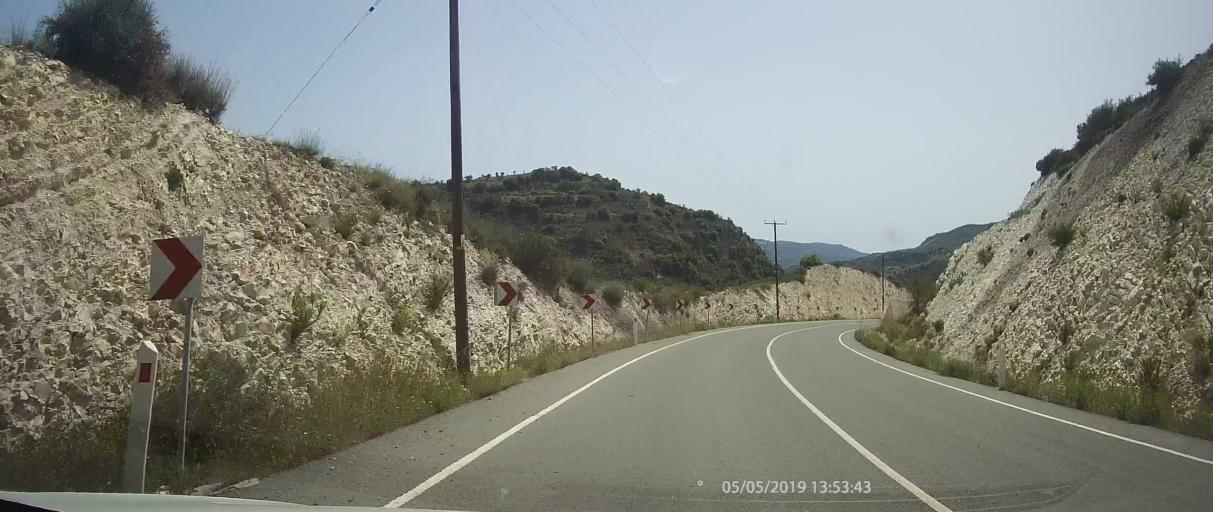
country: CY
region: Limassol
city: Pachna
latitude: 34.8171
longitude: 32.7251
